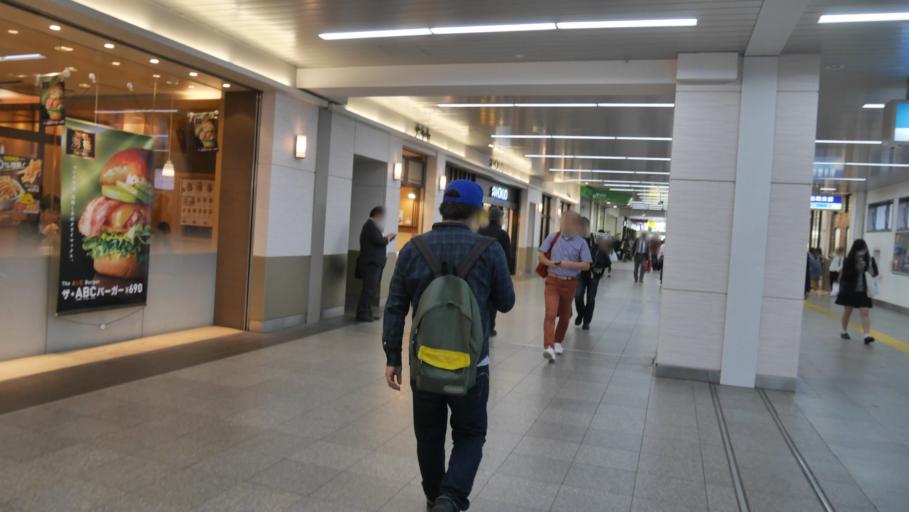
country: JP
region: Kanagawa
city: Kamakura
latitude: 35.3535
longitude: 139.5307
